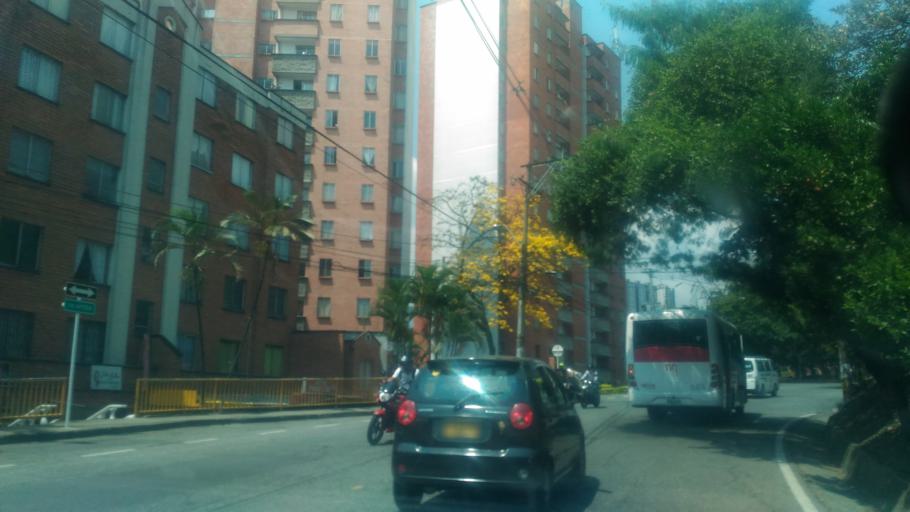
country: CO
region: Antioquia
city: Medellin
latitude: 6.2772
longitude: -75.5908
